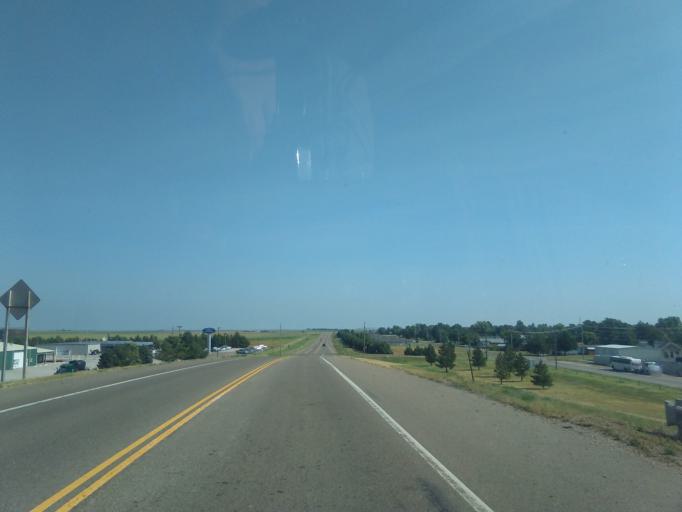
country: US
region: Kansas
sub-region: Sherman County
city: Goodland
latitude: 39.3408
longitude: -101.7268
